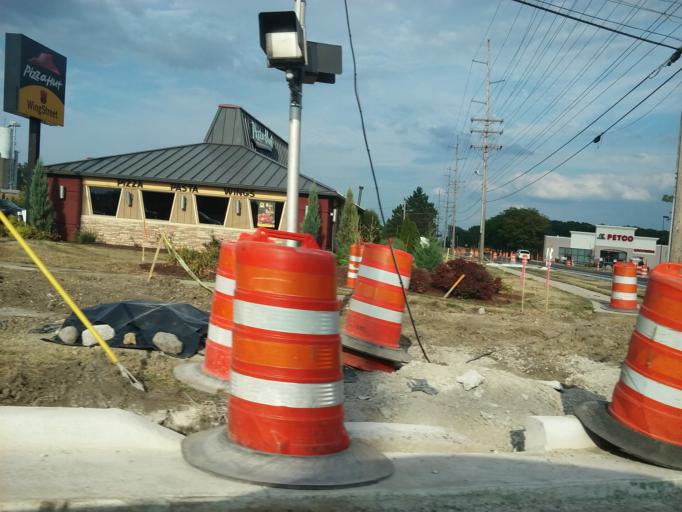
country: US
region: Ohio
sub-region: Wood County
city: Bowling Green
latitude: 41.3567
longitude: -83.6503
